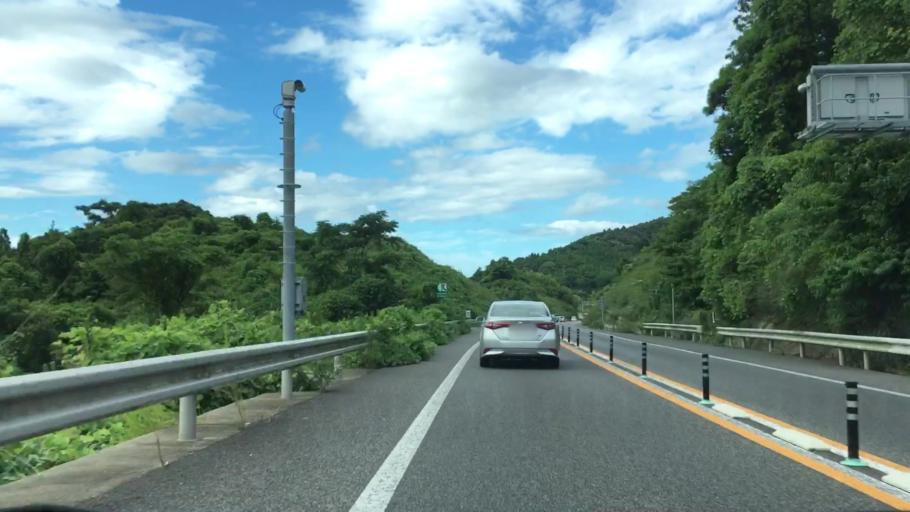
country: JP
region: Saga Prefecture
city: Karatsu
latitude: 33.4687
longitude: 130.0425
